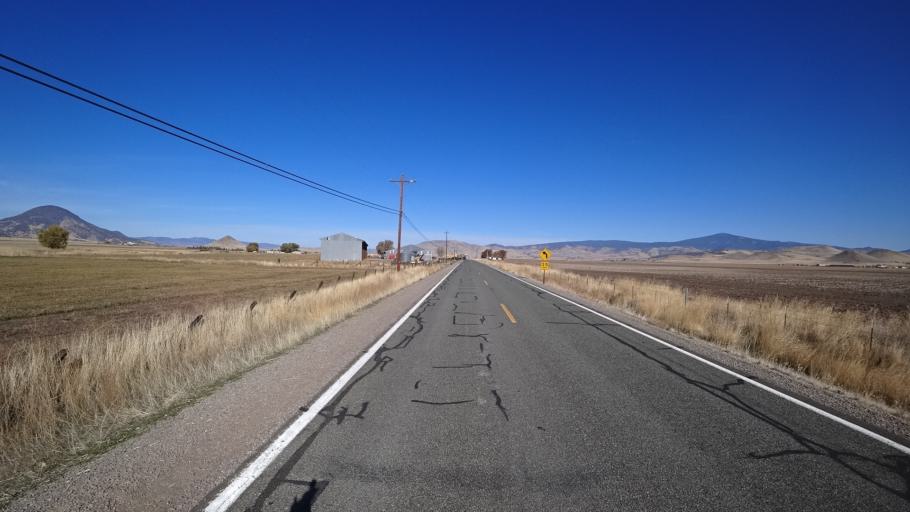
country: US
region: California
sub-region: Siskiyou County
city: Montague
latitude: 41.7753
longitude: -122.4758
